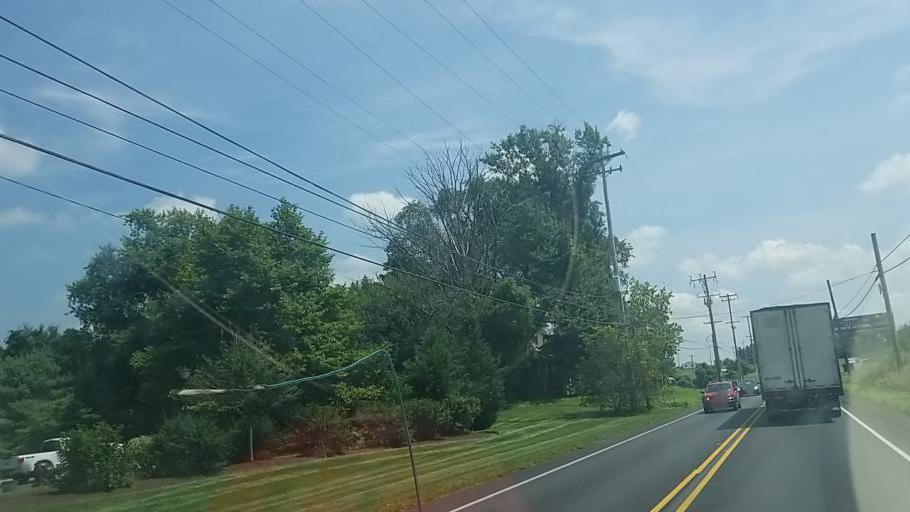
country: US
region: Pennsylvania
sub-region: Chester County
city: Toughkenamon
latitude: 39.8044
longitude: -75.7429
